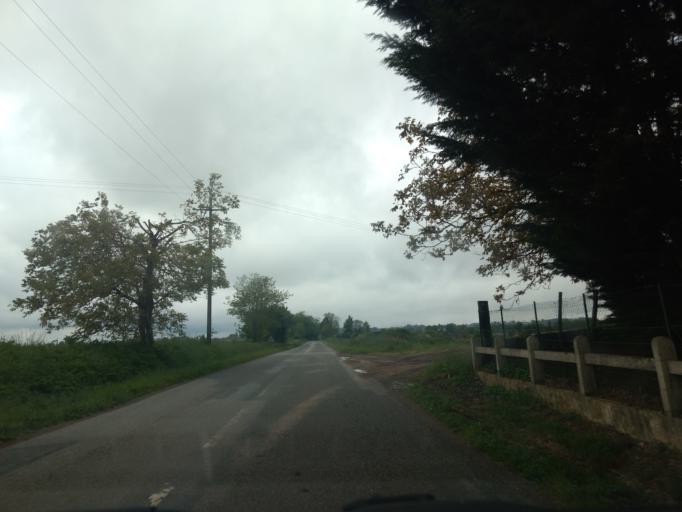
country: FR
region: Midi-Pyrenees
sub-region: Departement de l'Aveyron
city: Viviez
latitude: 44.5165
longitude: 2.1835
